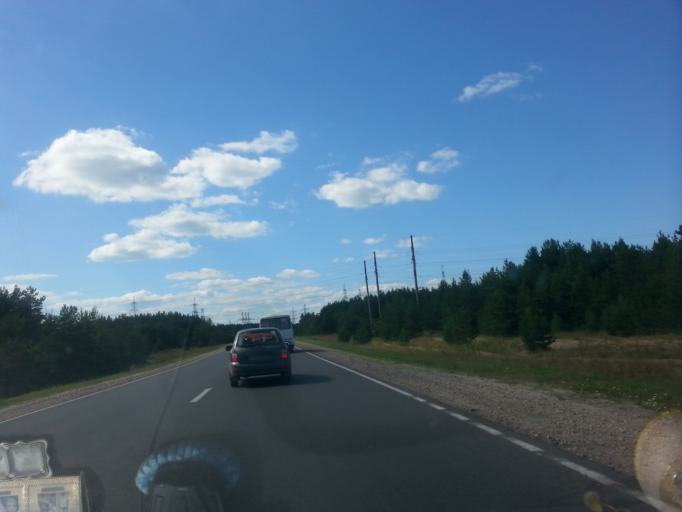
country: RU
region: Nizjnij Novgorod
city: Lukino
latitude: 56.3890
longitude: 43.7058
